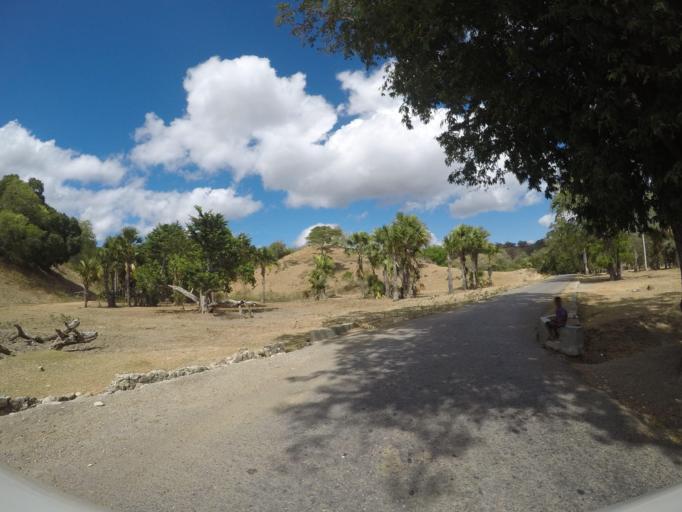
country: TL
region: Lautem
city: Lospalos
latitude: -8.4085
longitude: 126.8288
